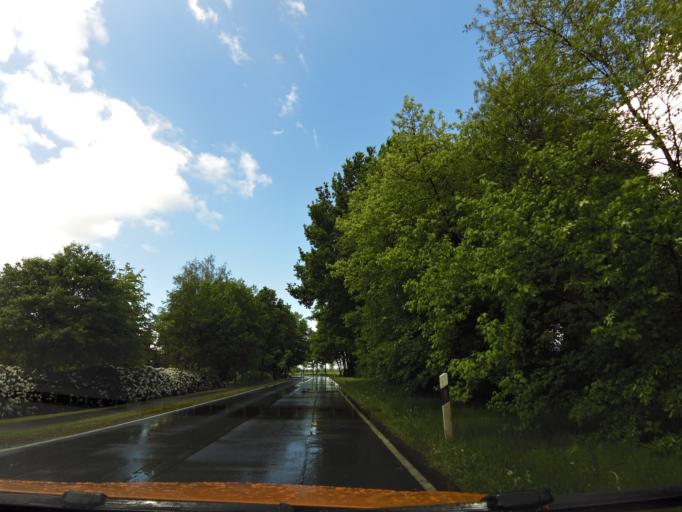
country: DE
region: Lower Saxony
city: Hatten
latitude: 53.1213
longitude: 8.3265
